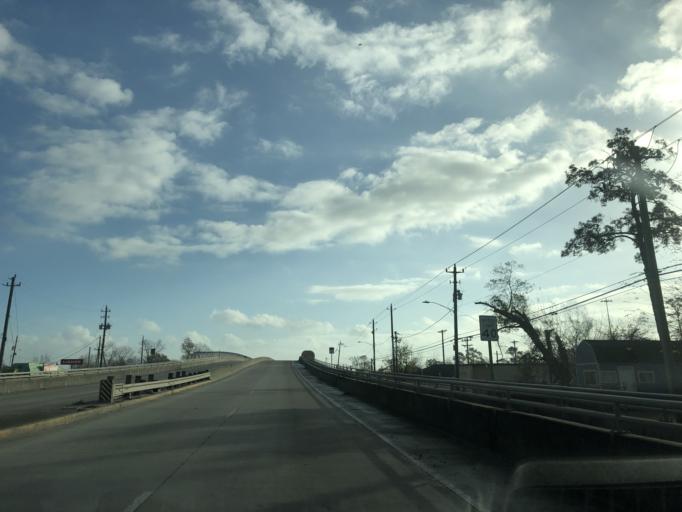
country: US
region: Texas
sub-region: Harris County
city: Jacinto City
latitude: 29.8313
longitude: -95.2911
